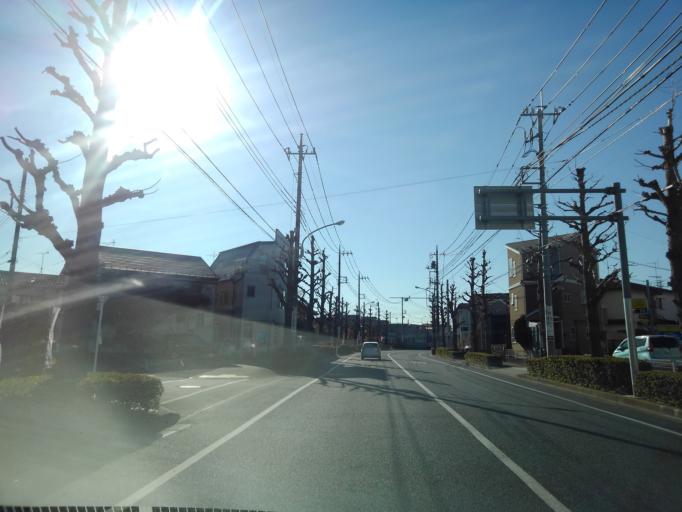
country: JP
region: Tokyo
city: Hino
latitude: 35.7218
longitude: 139.3836
